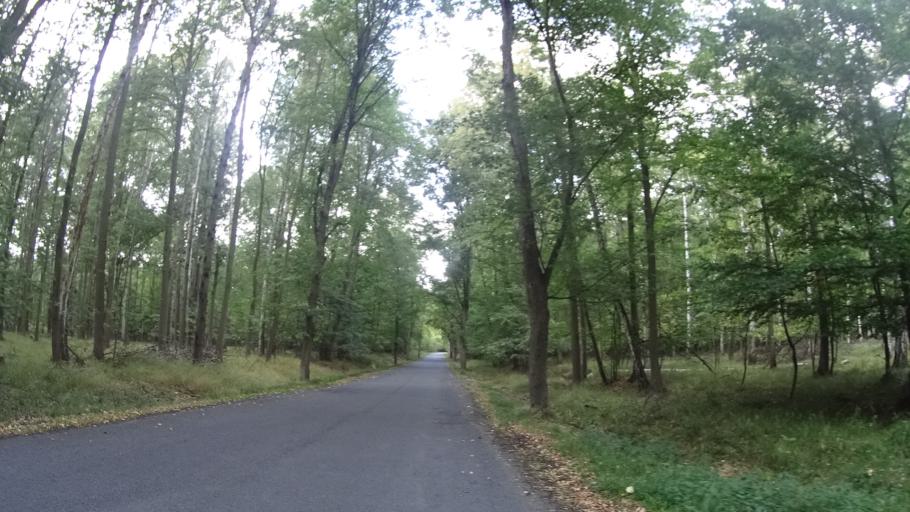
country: CZ
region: Olomoucky
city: Bila Lhota
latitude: 49.7286
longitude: 17.0126
